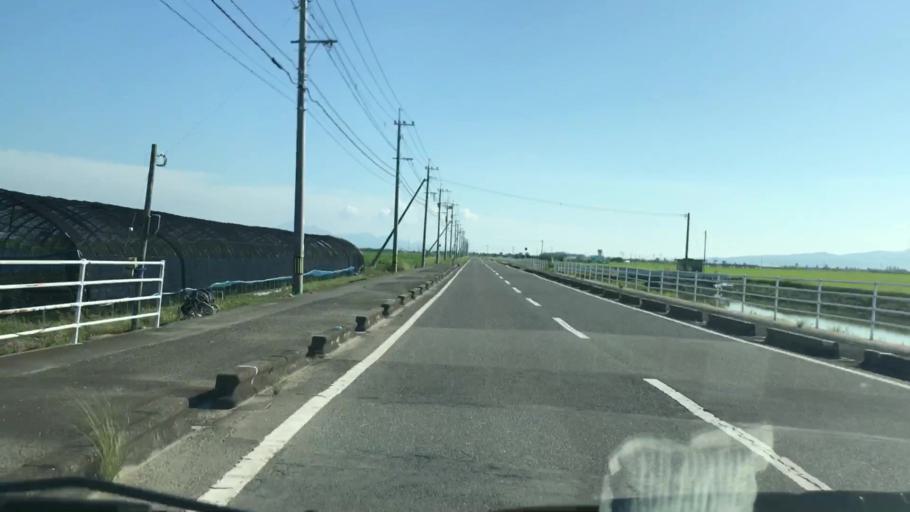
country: JP
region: Saga Prefecture
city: Okawa
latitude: 33.1730
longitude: 130.3111
